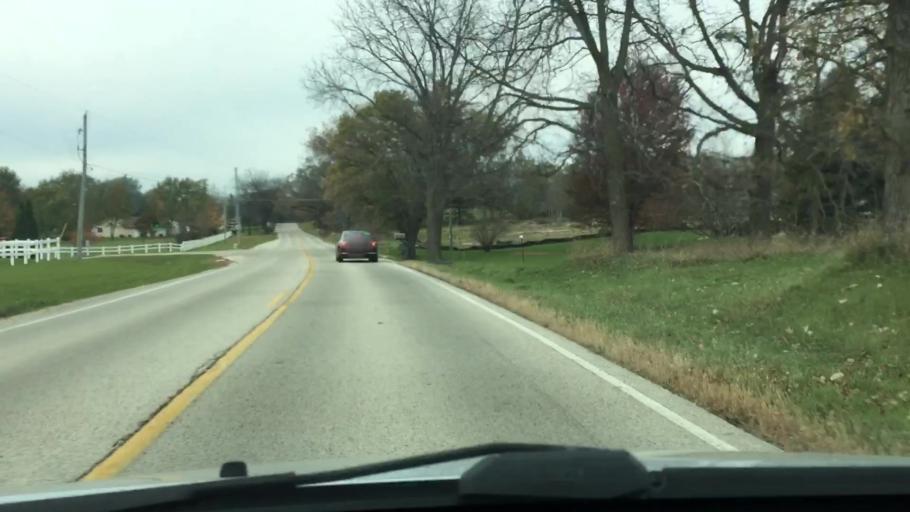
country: US
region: Wisconsin
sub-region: Waukesha County
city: North Prairie
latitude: 42.8971
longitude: -88.3950
